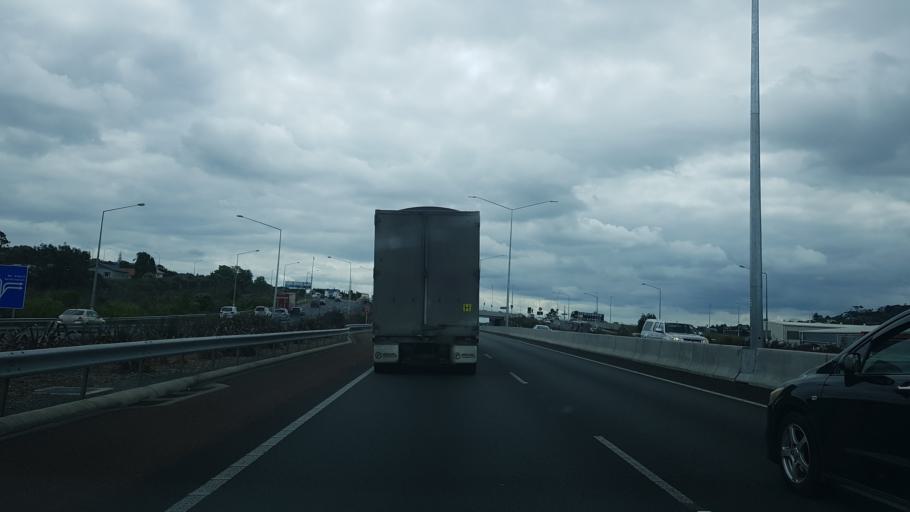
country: NZ
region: Auckland
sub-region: Auckland
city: Auckland
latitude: -36.9054
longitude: 174.7264
